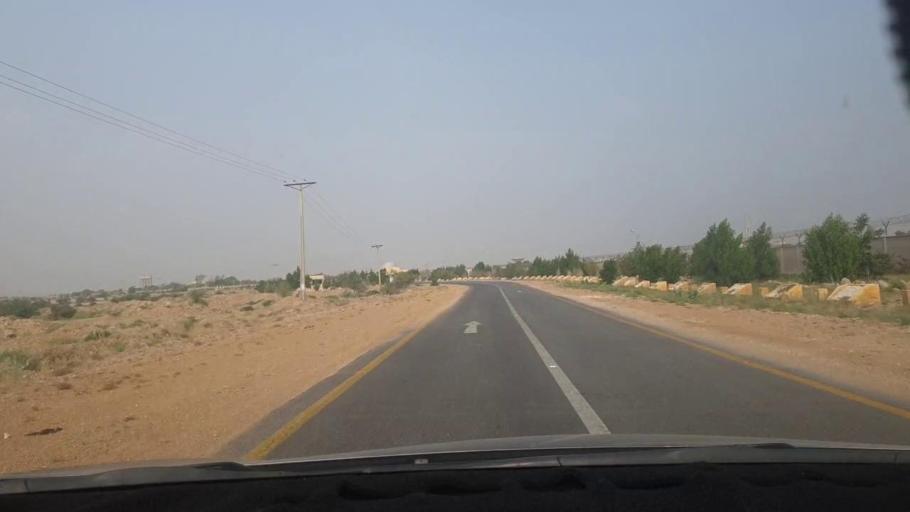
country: PK
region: Sindh
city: Jamshoro
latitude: 25.5515
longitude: 68.3200
